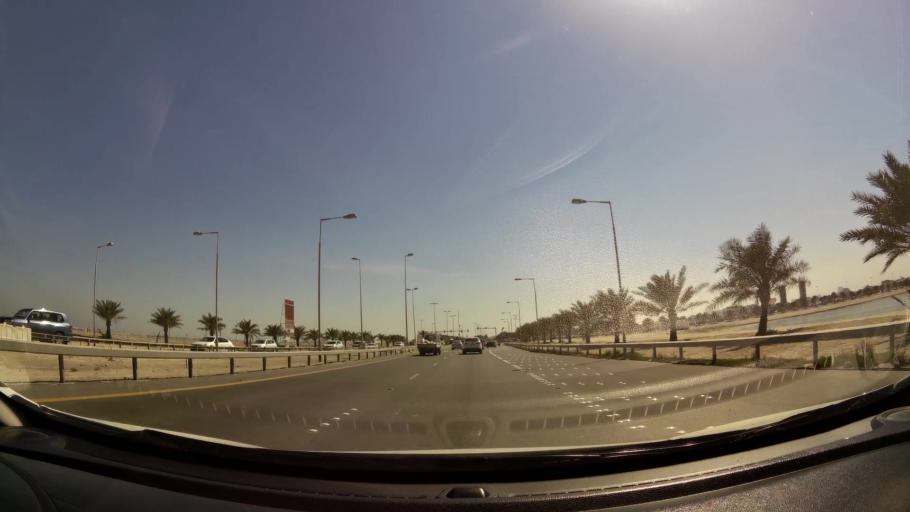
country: BH
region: Muharraq
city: Al Hadd
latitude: 26.2563
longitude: 50.6600
